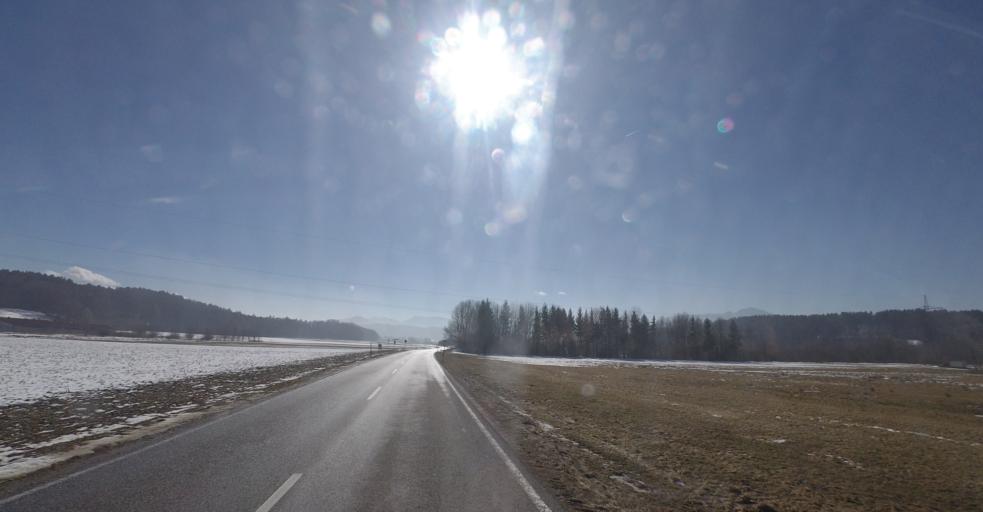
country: DE
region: Bavaria
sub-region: Upper Bavaria
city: Vachendorf
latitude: 47.8639
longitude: 12.5864
